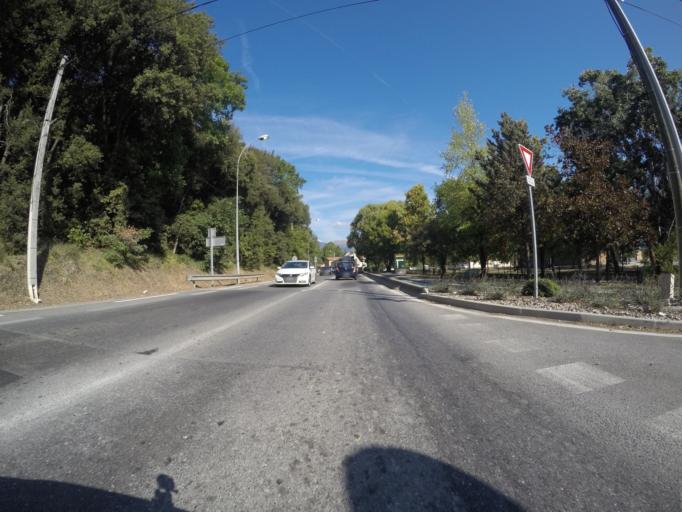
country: FR
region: Provence-Alpes-Cote d'Azur
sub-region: Departement des Alpes-Maritimes
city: Villeneuve-Loubet
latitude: 43.6548
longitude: 7.1250
